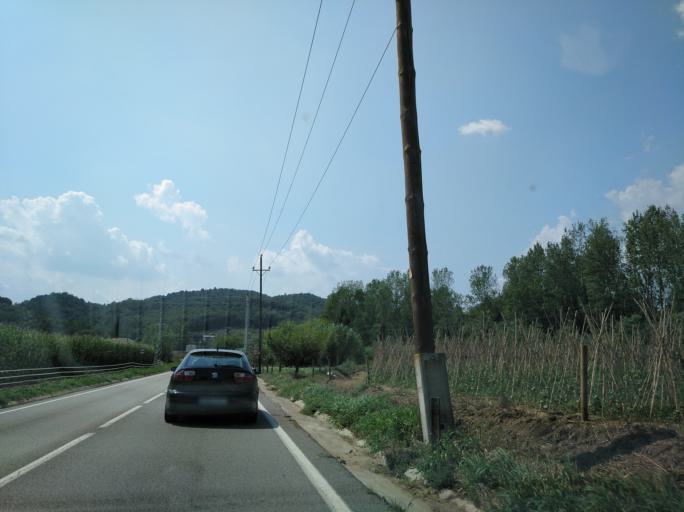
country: ES
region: Catalonia
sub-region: Provincia de Girona
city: Bescano
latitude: 41.9678
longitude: 2.7230
